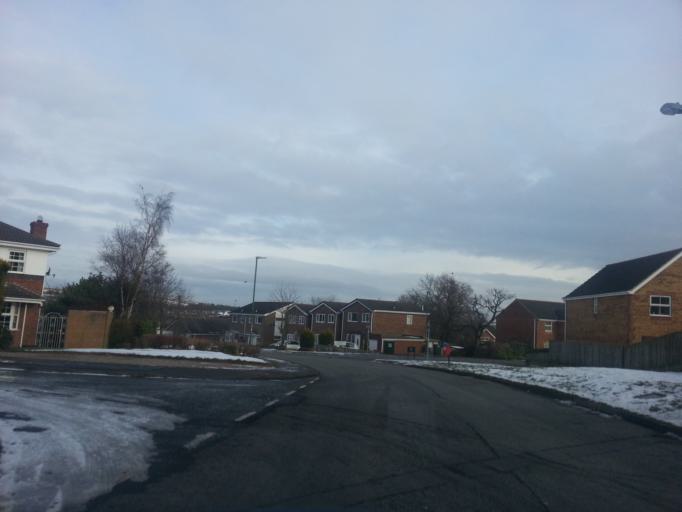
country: GB
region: England
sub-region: County Durham
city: Crook
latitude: 54.7084
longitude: -1.7613
